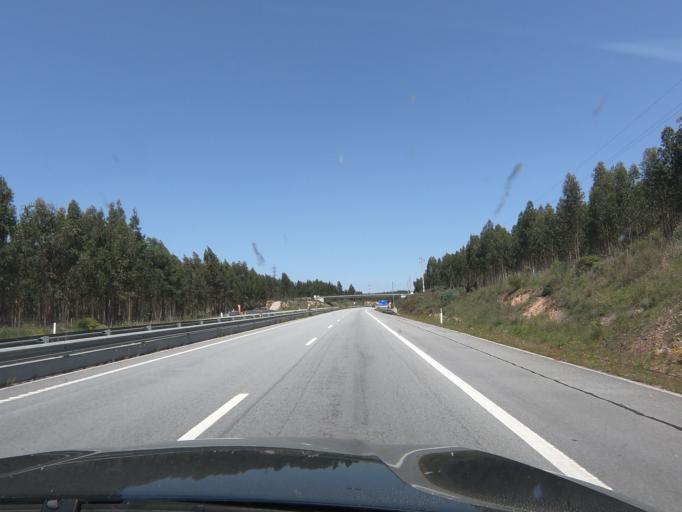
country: PT
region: Santarem
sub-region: Entroncamento
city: Entroncamento
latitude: 39.4976
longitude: -8.4396
